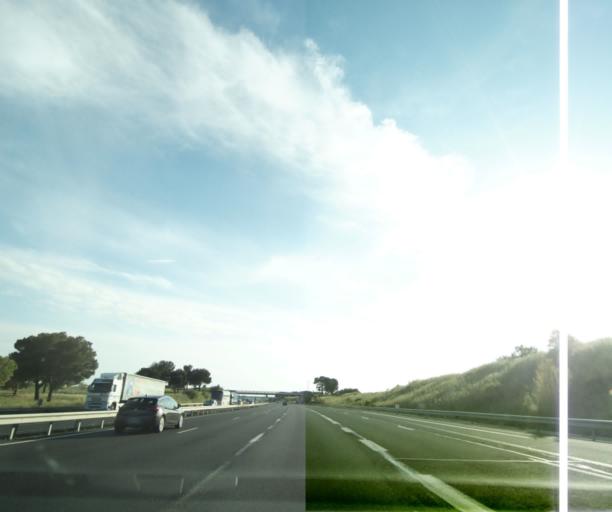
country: FR
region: Languedoc-Roussillon
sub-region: Departement de l'Herault
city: Cers
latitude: 43.3368
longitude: 3.2892
